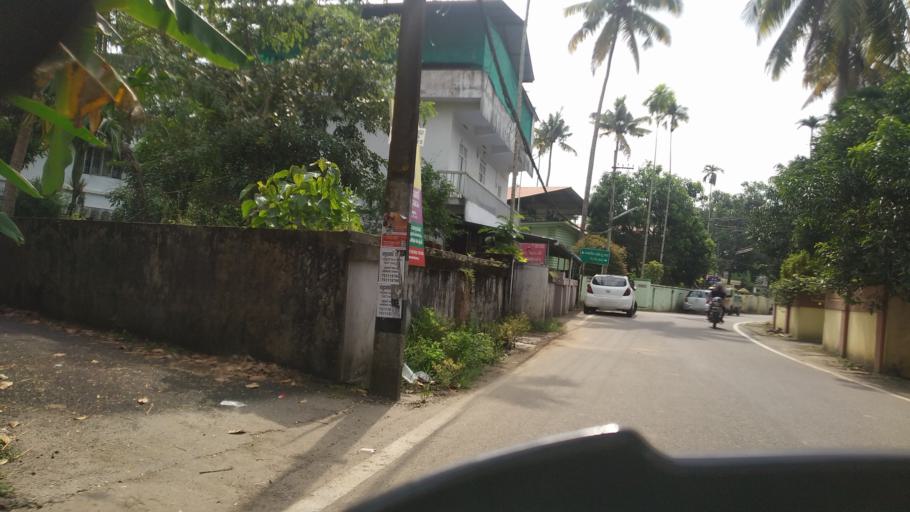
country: IN
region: Kerala
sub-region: Thrissur District
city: Kodungallur
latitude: 10.1442
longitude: 76.2326
